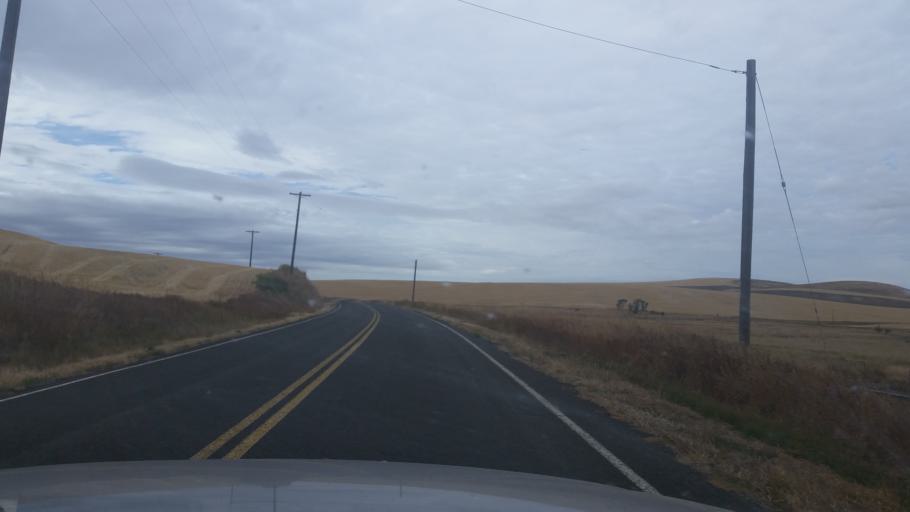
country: US
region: Washington
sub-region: Spokane County
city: Medical Lake
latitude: 47.5227
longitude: -117.9122
